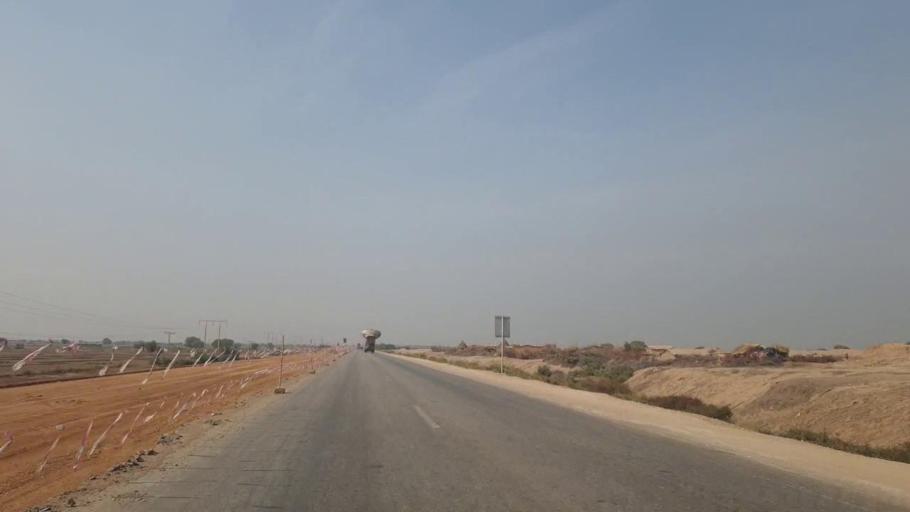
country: PK
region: Sindh
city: Sann
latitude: 26.1426
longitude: 68.0367
